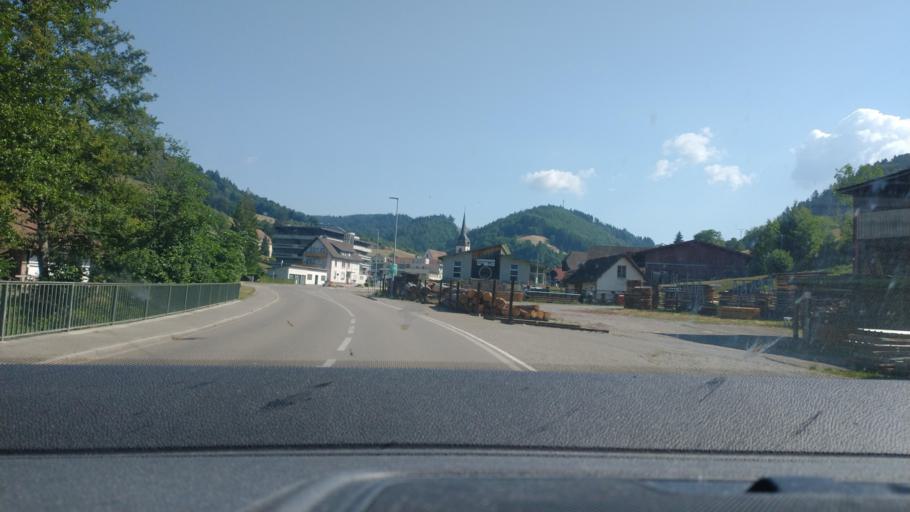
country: DE
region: Baden-Wuerttemberg
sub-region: Freiburg Region
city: Nordrach
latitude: 48.3941
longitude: 8.0756
